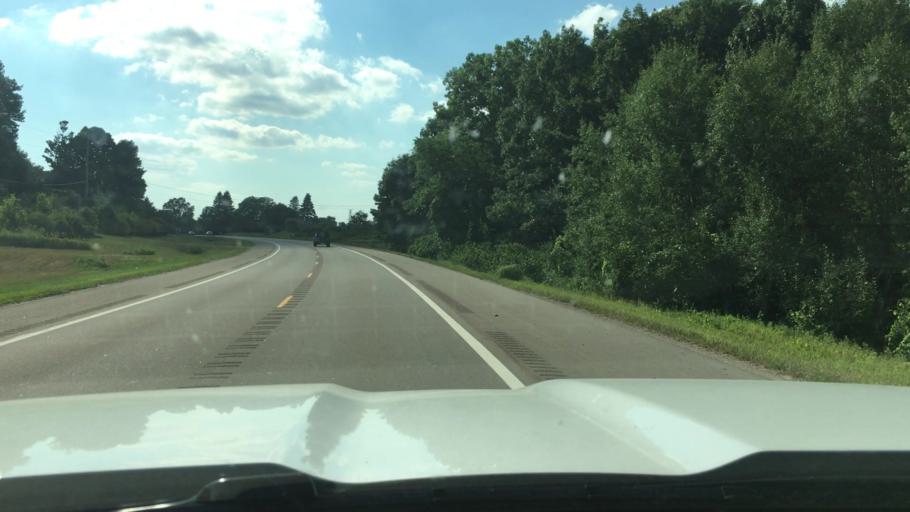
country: US
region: Michigan
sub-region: Kent County
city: Rockford
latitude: 43.0864
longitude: -85.4234
